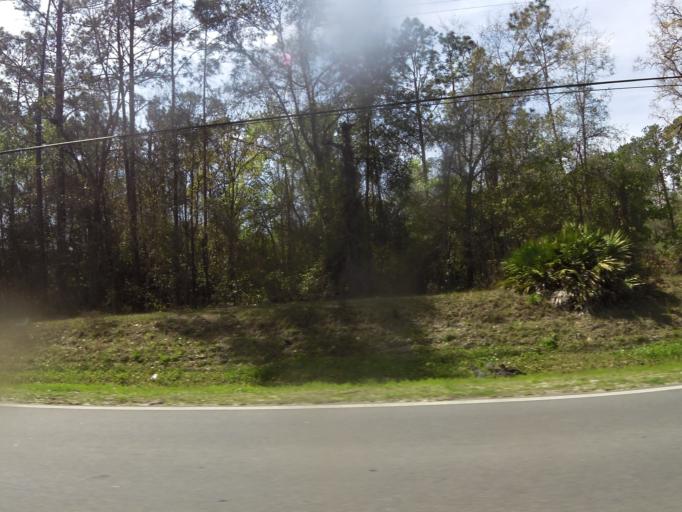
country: US
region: Florida
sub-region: Clay County
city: Middleburg
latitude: 30.1058
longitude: -81.8646
